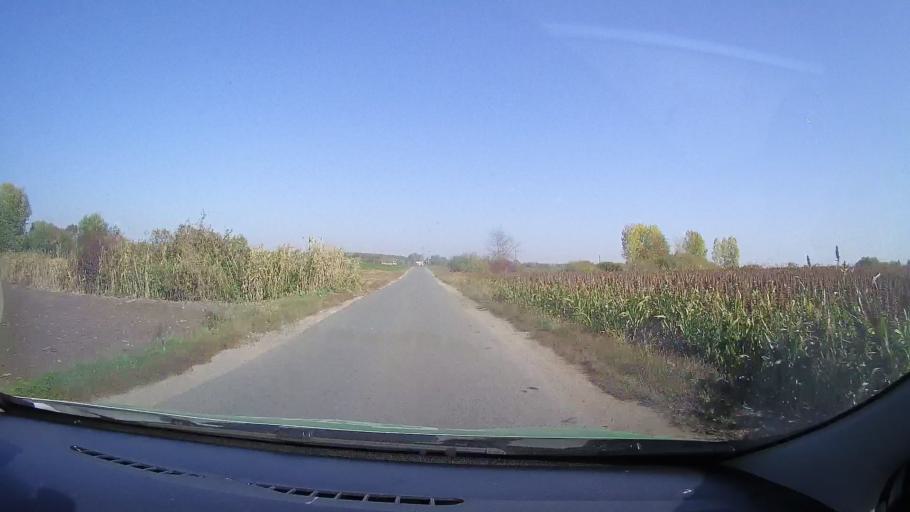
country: RO
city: Foieni
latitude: 47.6957
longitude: 22.3584
